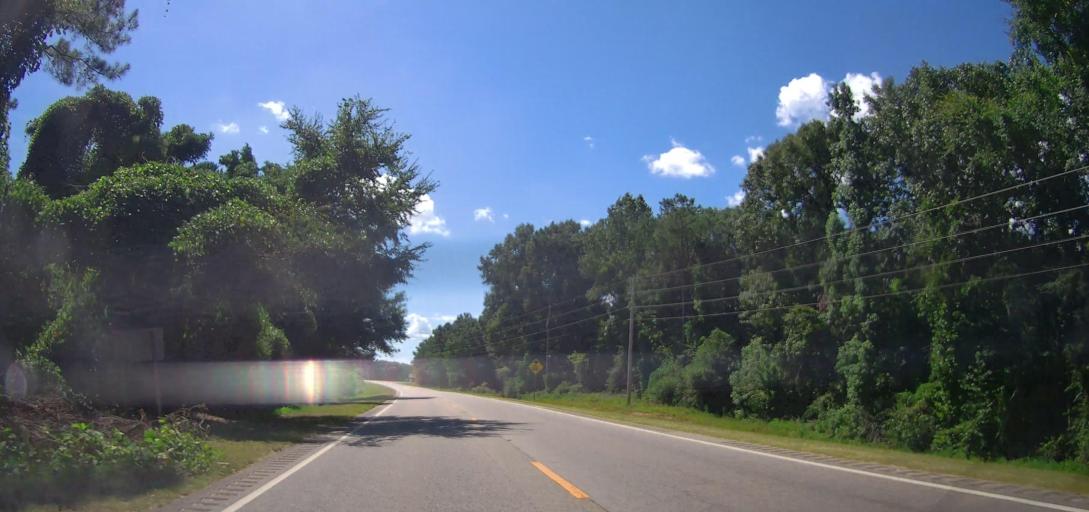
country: US
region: Alabama
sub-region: Elmore County
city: Tallassee
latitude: 32.3972
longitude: -85.9127
